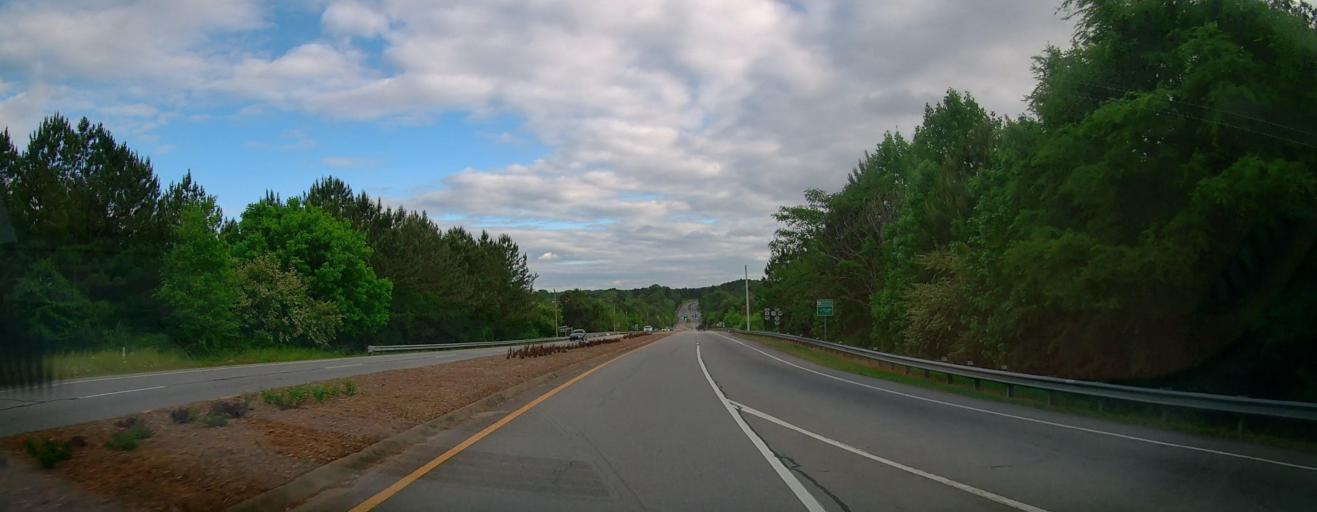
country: US
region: Georgia
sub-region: Clarke County
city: Athens
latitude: 33.9181
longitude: -83.4055
